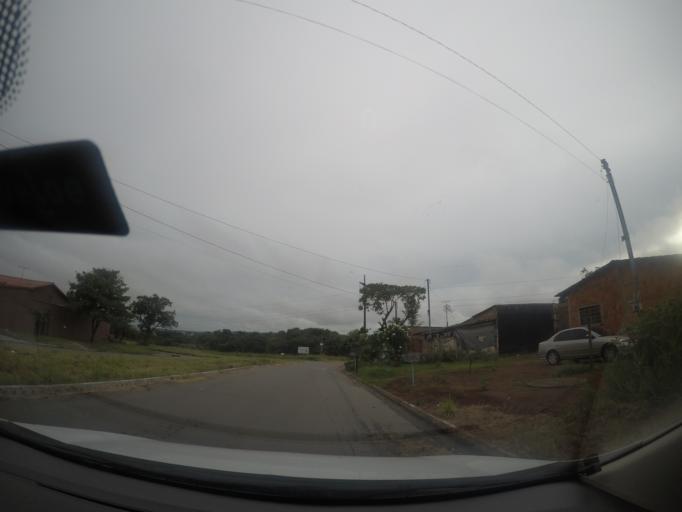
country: BR
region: Goias
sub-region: Aparecida De Goiania
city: Aparecida de Goiania
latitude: -16.7555
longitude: -49.3127
